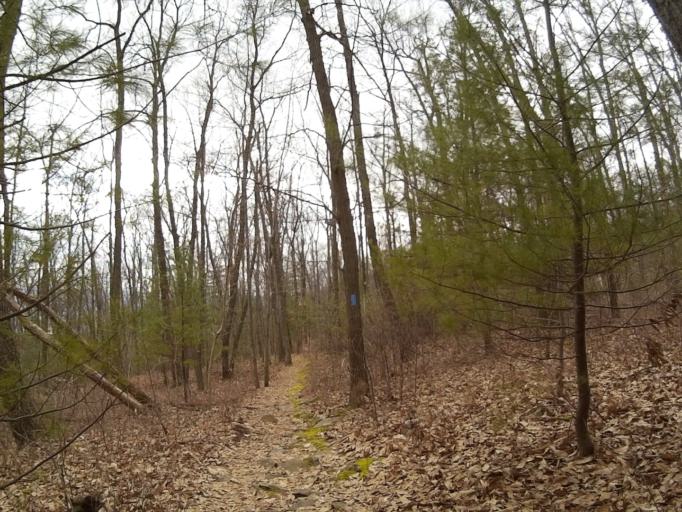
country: US
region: Pennsylvania
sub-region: Centre County
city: Lemont
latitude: 40.8099
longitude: -77.7934
